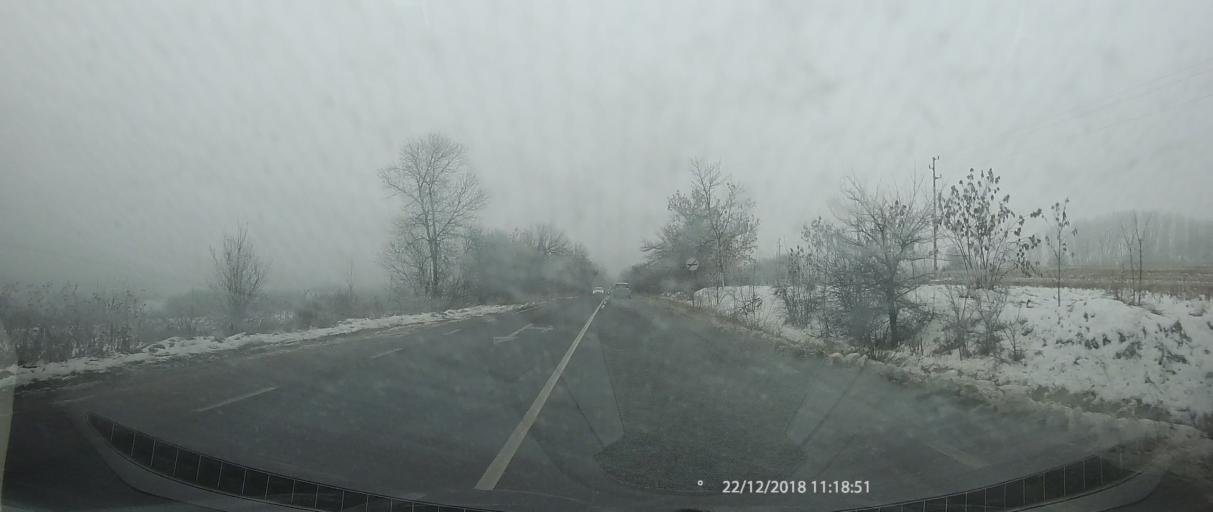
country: BG
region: Kyustendil
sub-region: Obshtina Kyustendil
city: Kyustendil
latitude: 42.2703
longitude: 22.7860
